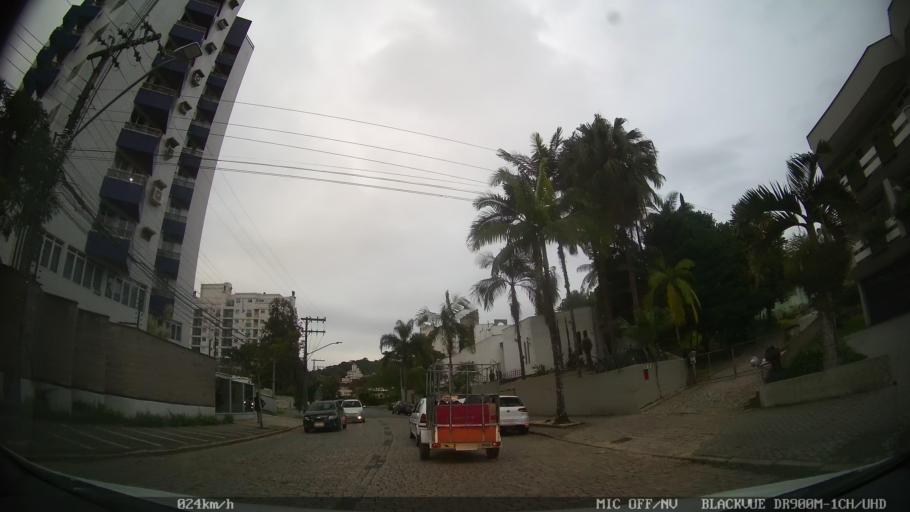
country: BR
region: Santa Catarina
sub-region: Joinville
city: Joinville
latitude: -26.3072
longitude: -48.8567
